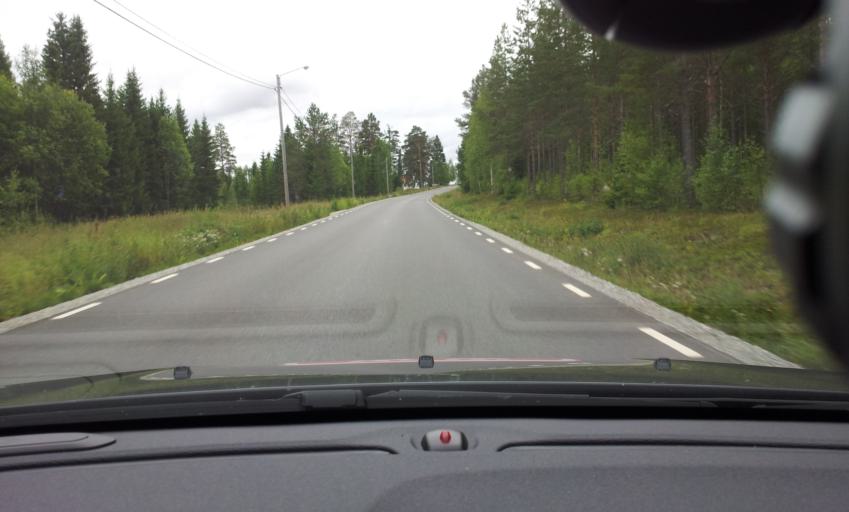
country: SE
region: Jaemtland
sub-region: Braecke Kommun
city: Braecke
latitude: 63.1191
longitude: 15.4878
